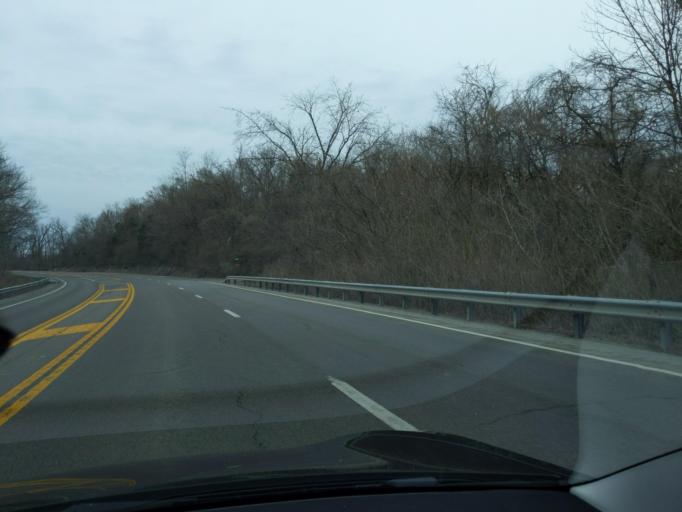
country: US
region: Kentucky
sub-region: Madison County
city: Richmond
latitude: 37.8895
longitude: -84.2843
